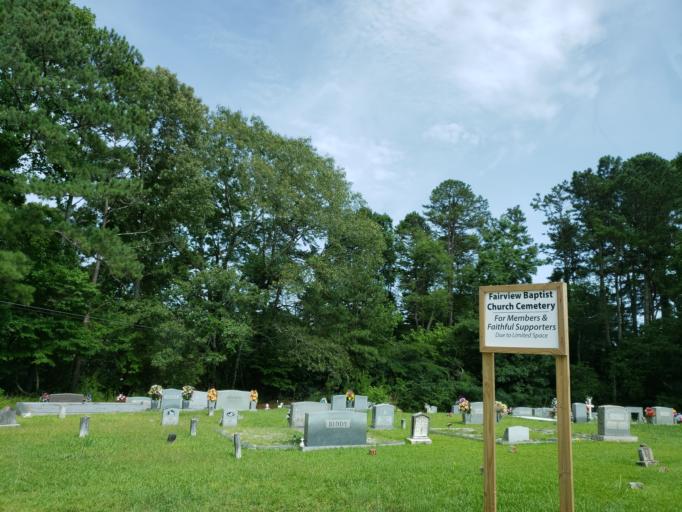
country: US
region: Georgia
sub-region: Pickens County
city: Nelson
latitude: 34.3725
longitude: -84.3847
